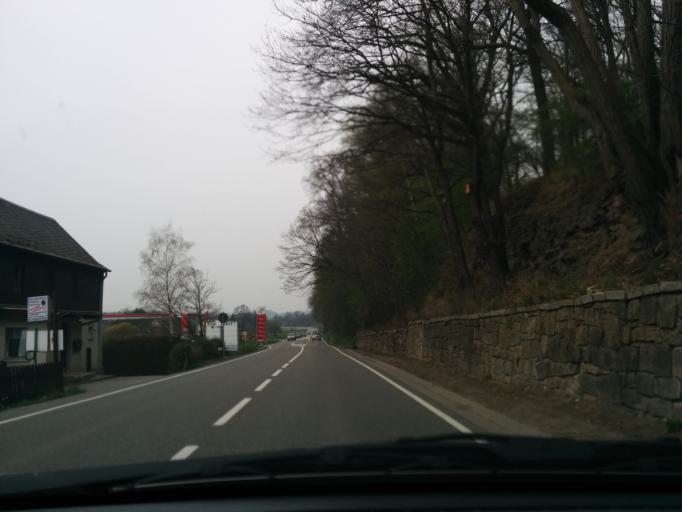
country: DE
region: Saxony
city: Floha
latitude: 50.8640
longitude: 13.0594
